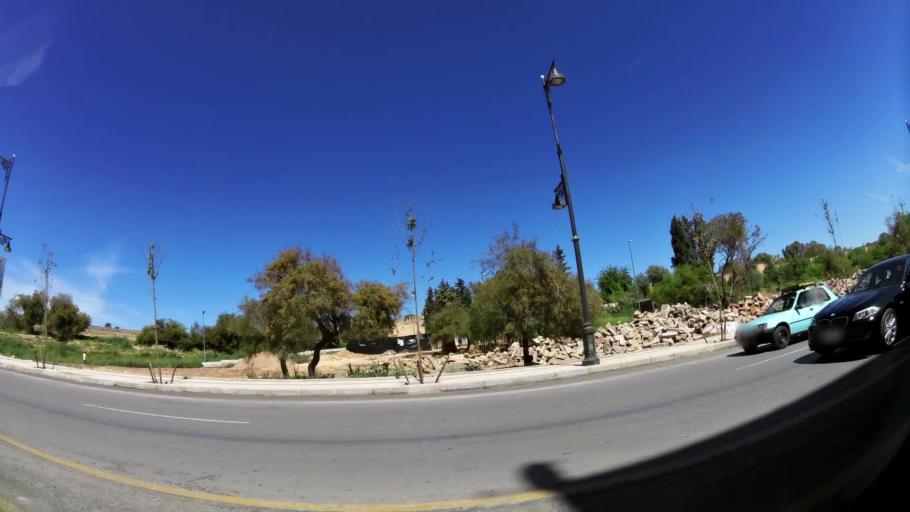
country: MA
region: Meknes-Tafilalet
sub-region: Meknes
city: Meknes
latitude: 33.8704
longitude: -5.5386
